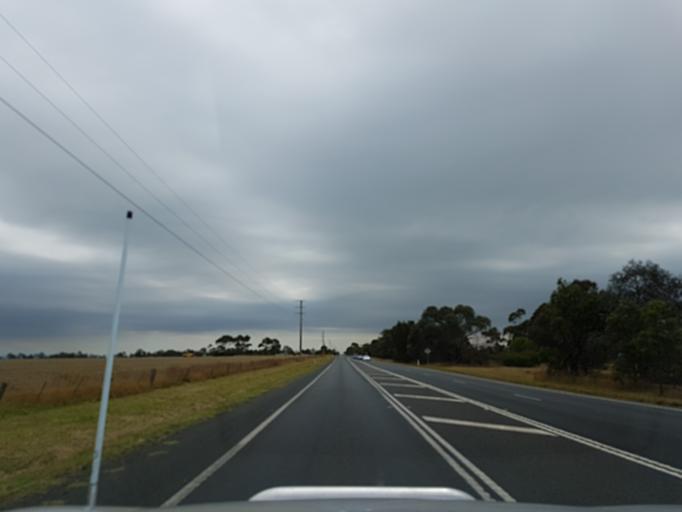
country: AU
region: Victoria
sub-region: Wellington
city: Sale
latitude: -38.1043
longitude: 146.9236
